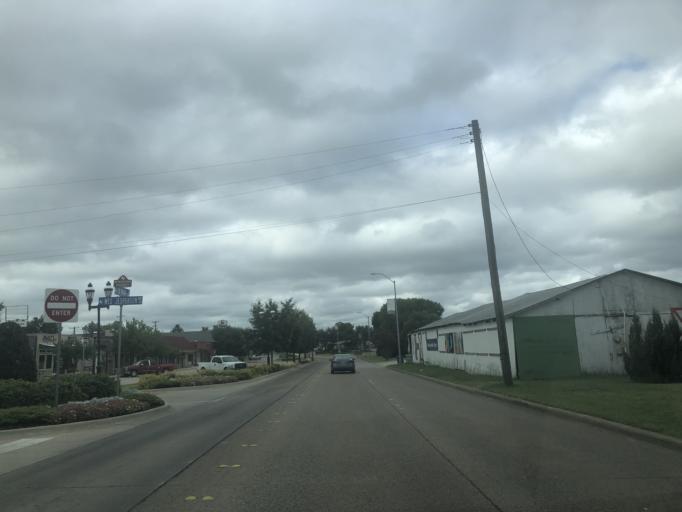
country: US
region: Texas
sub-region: Dallas County
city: Duncanville
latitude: 32.6540
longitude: -96.9082
